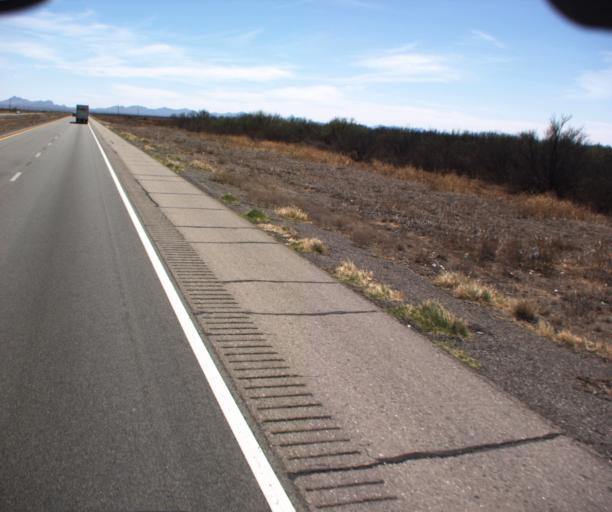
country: US
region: Arizona
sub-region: Cochise County
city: Willcox
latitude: 32.2865
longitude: -109.3077
